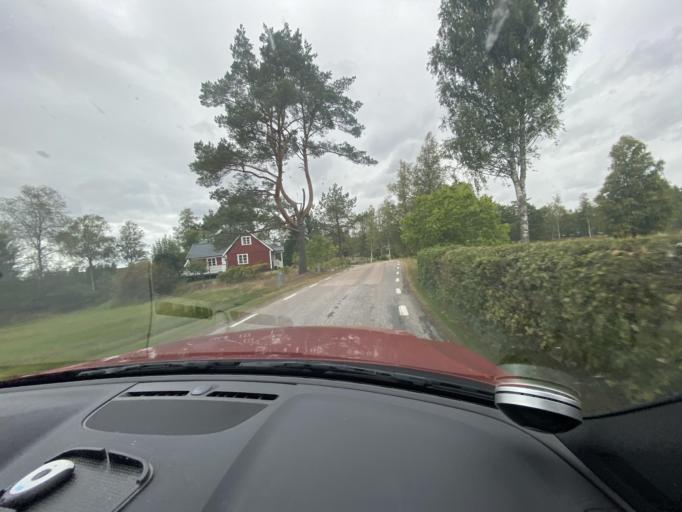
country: SE
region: Kronoberg
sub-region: Markaryds Kommun
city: Markaryd
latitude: 56.5005
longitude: 13.5655
